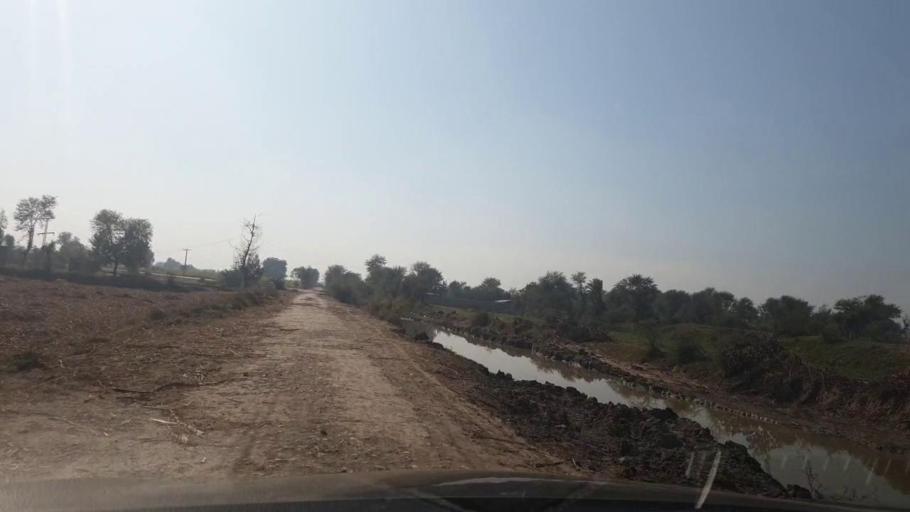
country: PK
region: Sindh
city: Ubauro
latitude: 28.1492
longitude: 69.6914
